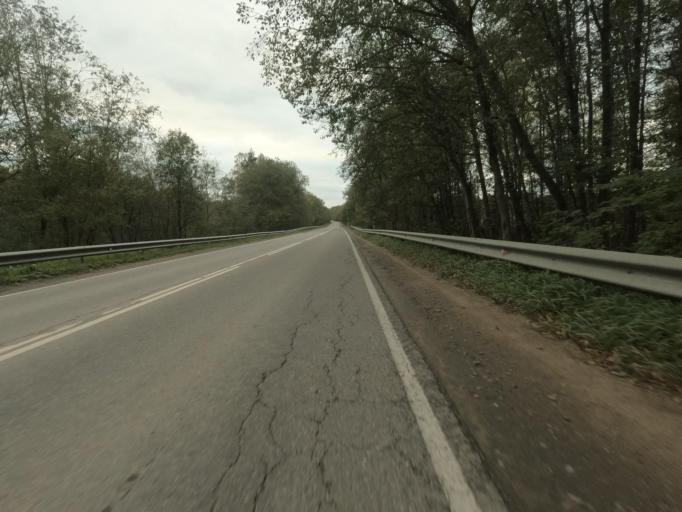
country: RU
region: Leningrad
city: Pavlovo
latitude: 59.7926
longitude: 30.9578
